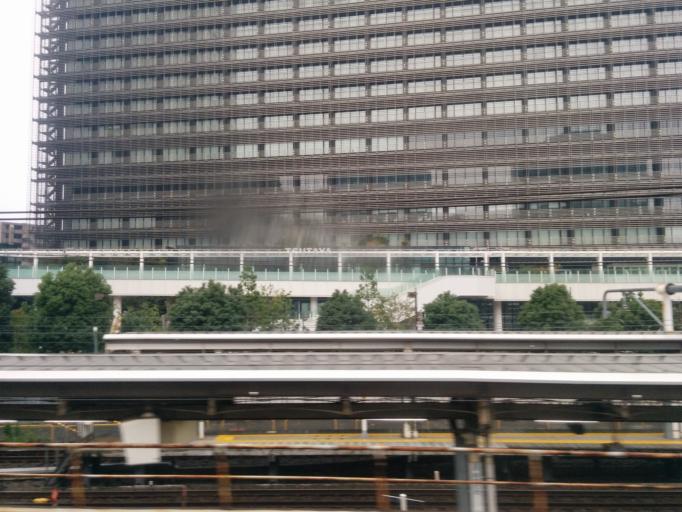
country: JP
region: Tokyo
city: Tokyo
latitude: 35.6179
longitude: 139.7294
